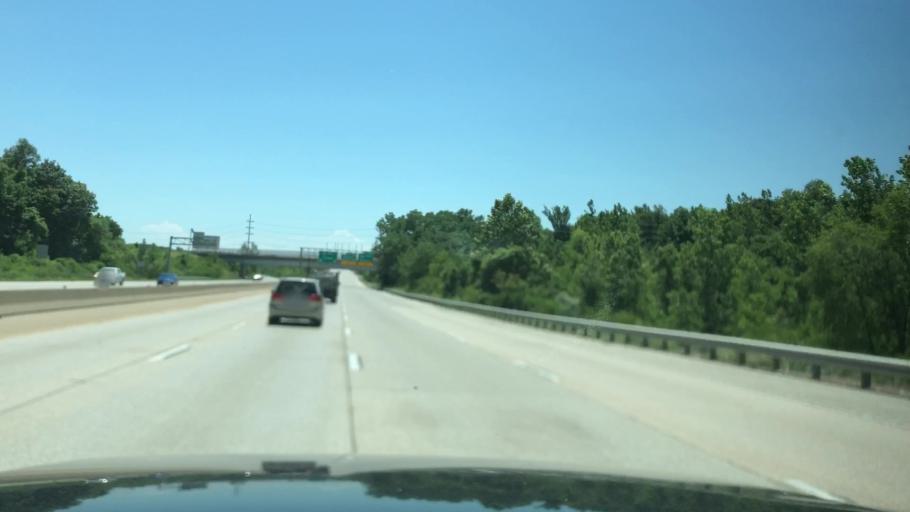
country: US
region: Missouri
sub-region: Saint Louis County
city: Bridgeton
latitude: 38.7771
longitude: -90.4142
